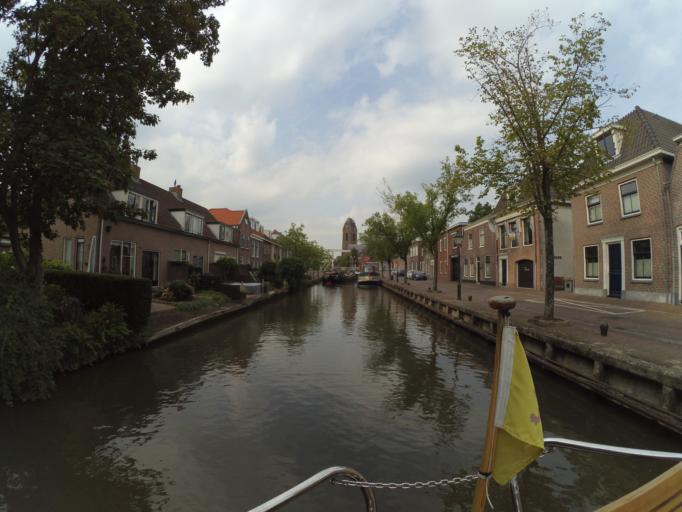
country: NL
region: Utrecht
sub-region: Gemeente IJsselstein
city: IJsselstein
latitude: 52.0336
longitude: 5.0355
